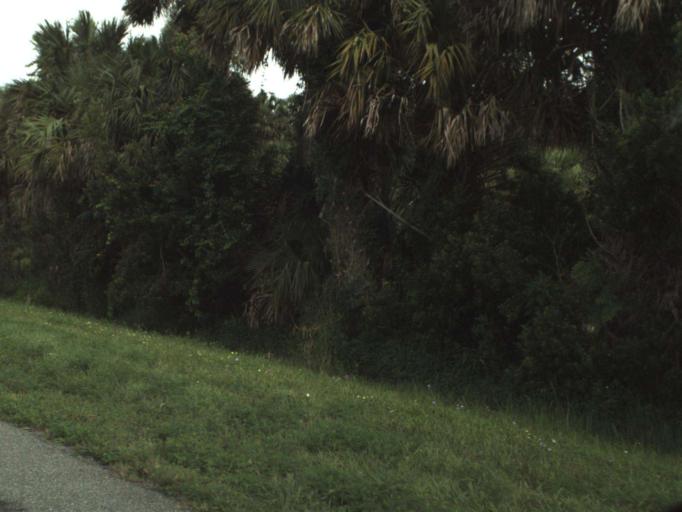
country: US
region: Florida
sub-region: Seminole County
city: Geneva
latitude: 28.7183
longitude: -81.0716
